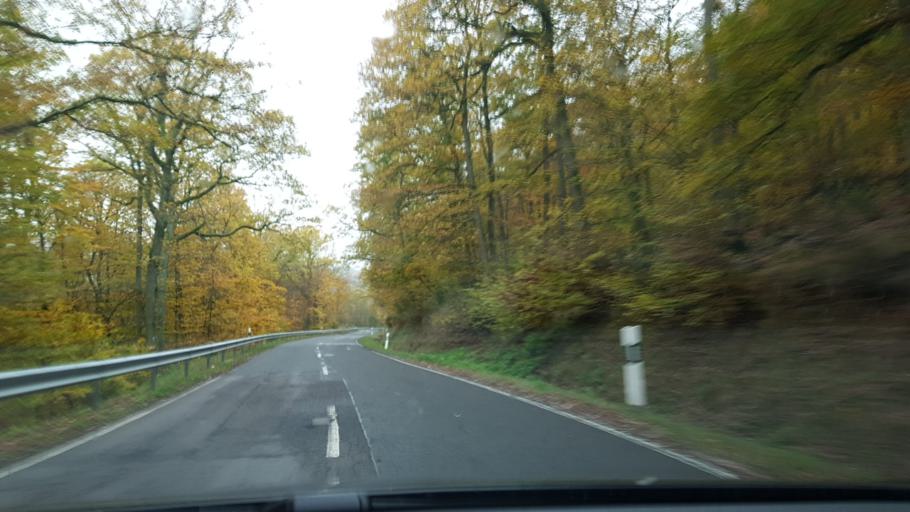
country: DE
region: Rheinland-Pfalz
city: Mehring
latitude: 49.7739
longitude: 6.8191
